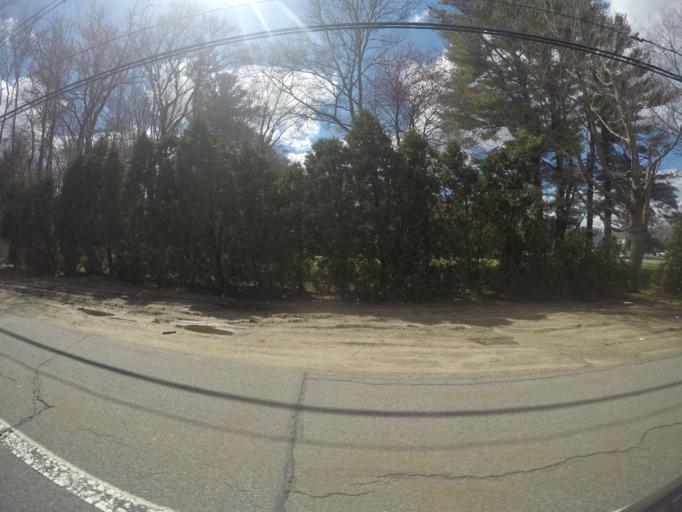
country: US
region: Massachusetts
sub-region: Bristol County
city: Raynham
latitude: 42.0029
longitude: -71.0669
